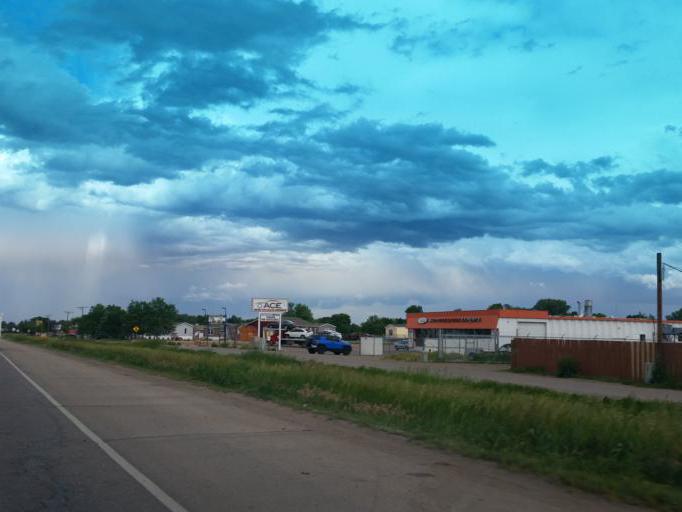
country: US
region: Colorado
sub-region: Larimer County
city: Fort Collins
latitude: 40.5810
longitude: -105.0485
